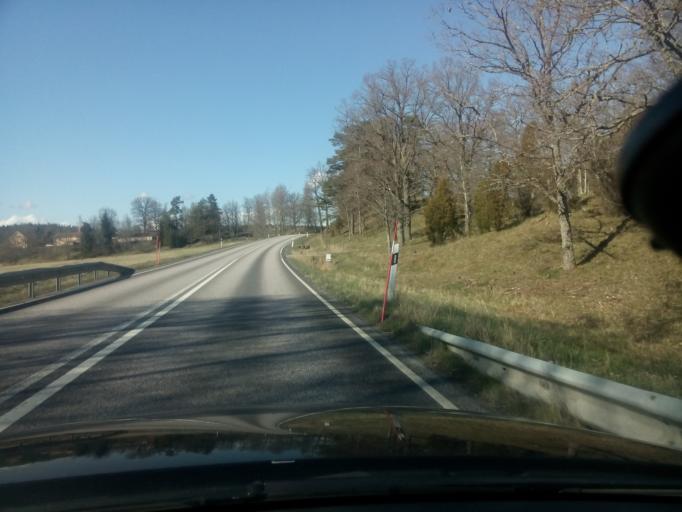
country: SE
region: Soedermanland
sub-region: Flens Kommun
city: Malmkoping
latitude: 58.9903
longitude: 16.8420
